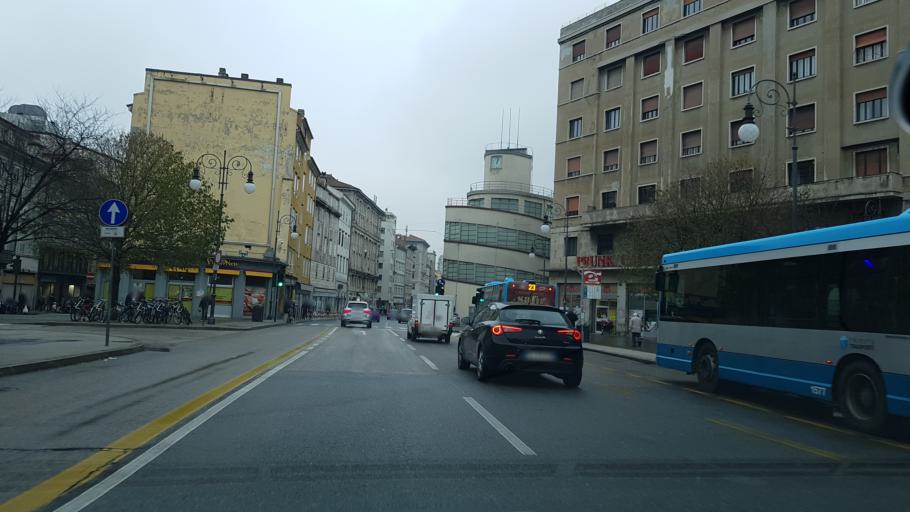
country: IT
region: Friuli Venezia Giulia
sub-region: Provincia di Trieste
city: Trieste
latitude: 45.6481
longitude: 13.7790
